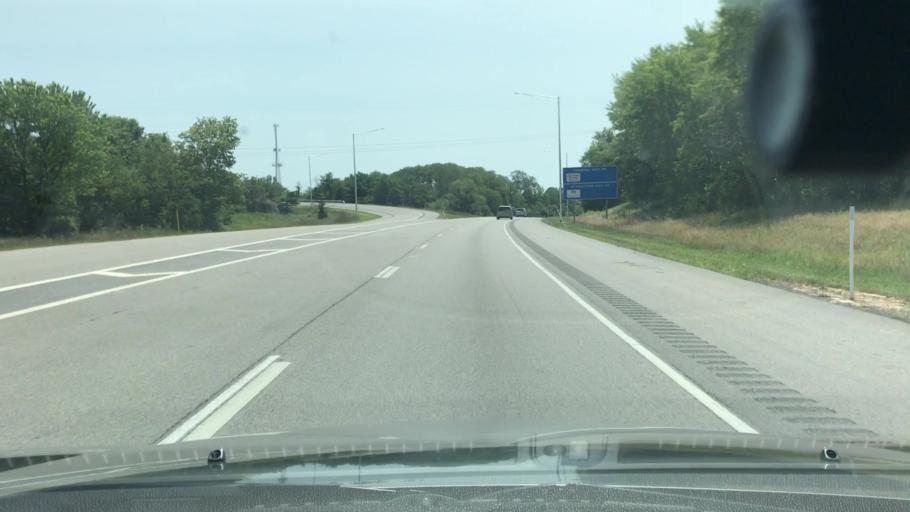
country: US
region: Illinois
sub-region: Jefferson County
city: Mount Vernon
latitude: 38.3378
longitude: -88.9603
